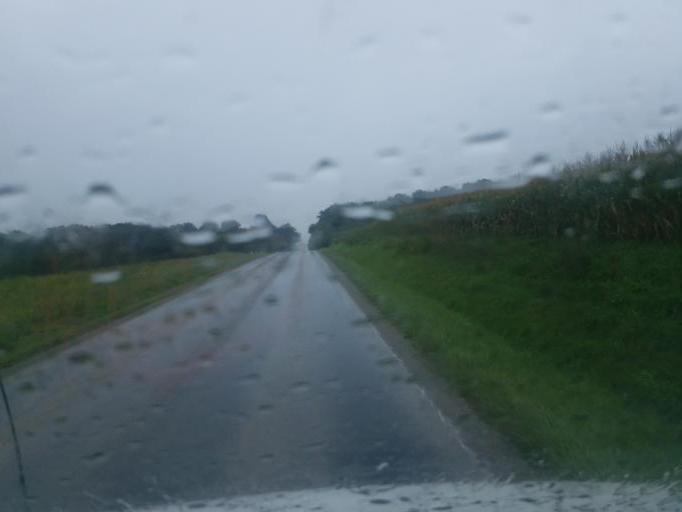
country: US
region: Ohio
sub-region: Wayne County
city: Creston
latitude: 40.9743
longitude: -81.9348
